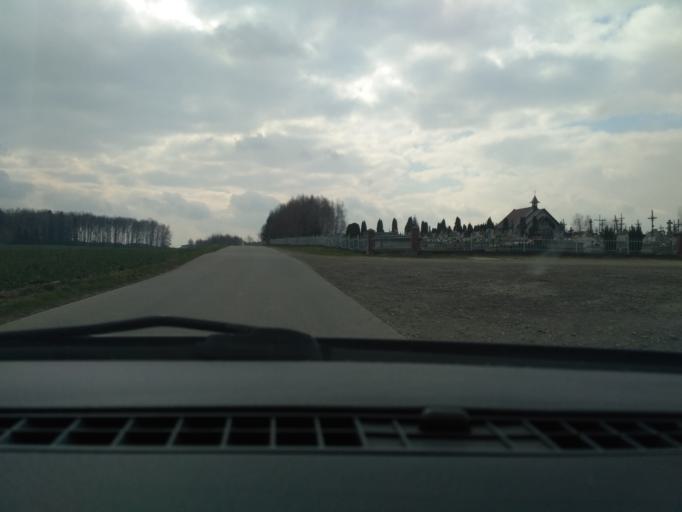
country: PL
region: Subcarpathian Voivodeship
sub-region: Powiat krosnienski
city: Kroscienko Wyzne
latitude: 49.6725
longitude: 21.8275
